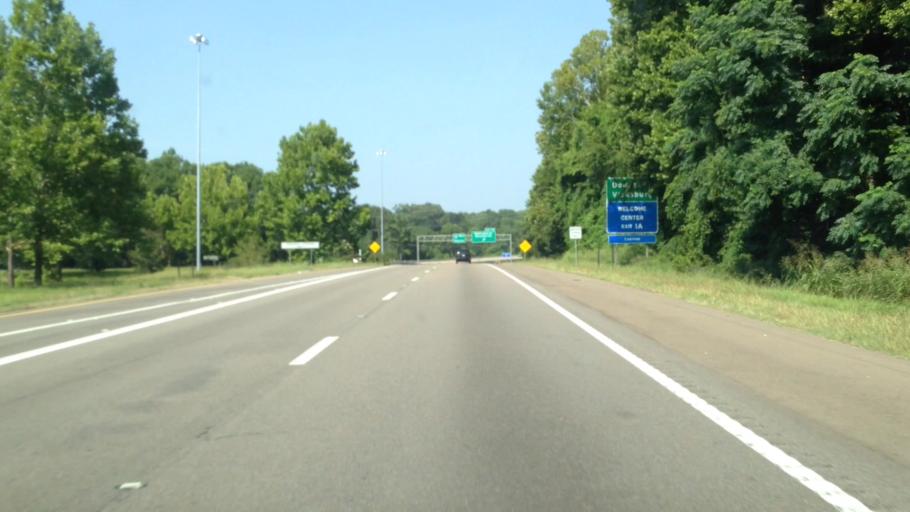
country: US
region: Mississippi
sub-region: Warren County
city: Vicksburg
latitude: 32.3118
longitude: -90.8920
